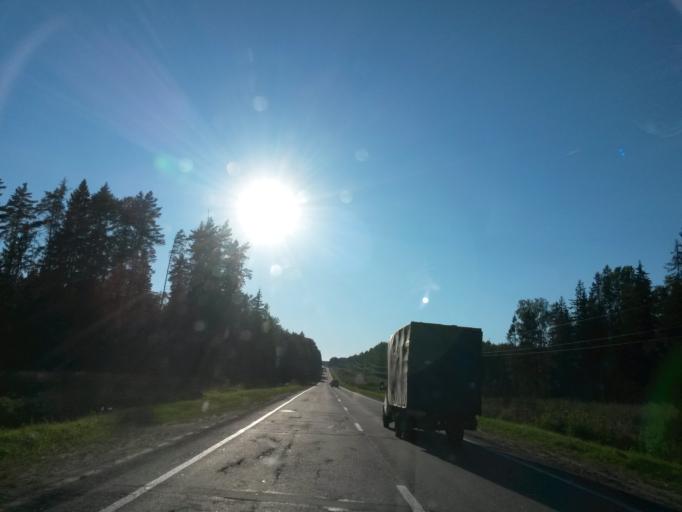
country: RU
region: Jaroslavl
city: Gavrilov-Yam
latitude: 57.2666
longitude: 39.9949
